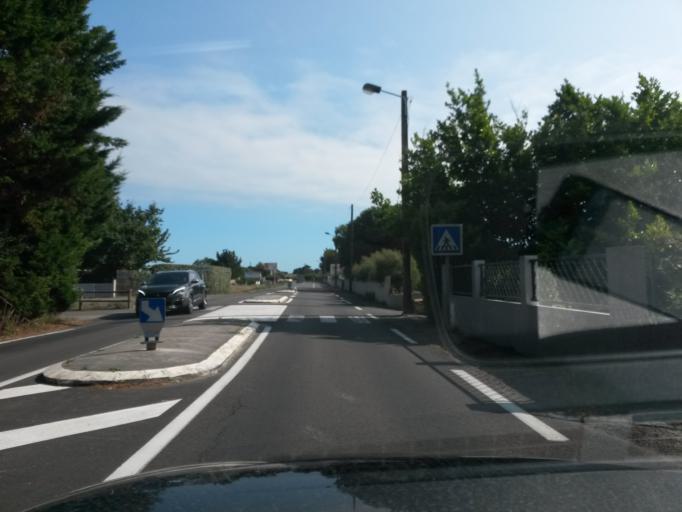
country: FR
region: Pays de la Loire
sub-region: Departement de la Vendee
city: Olonne-sur-Mer
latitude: 46.5567
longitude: -1.8113
